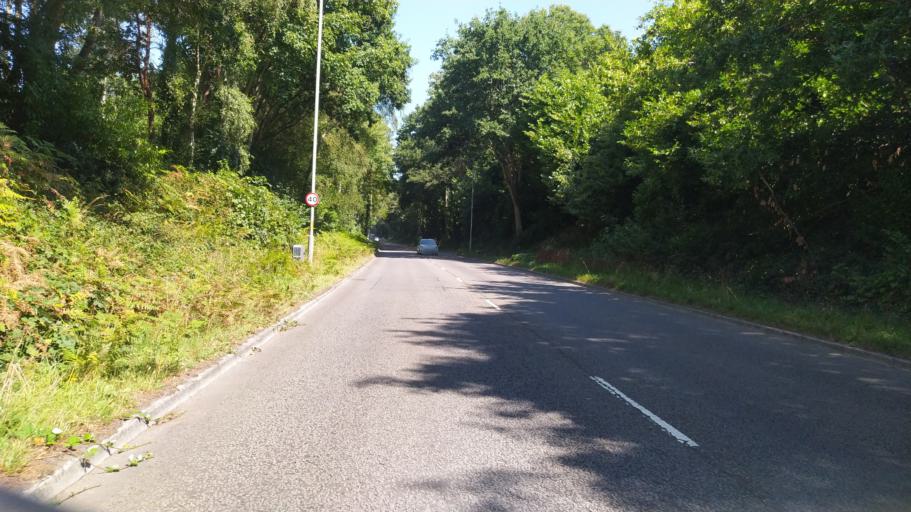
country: GB
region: England
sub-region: Dorset
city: Broadstone
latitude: 50.7553
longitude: -2.0000
